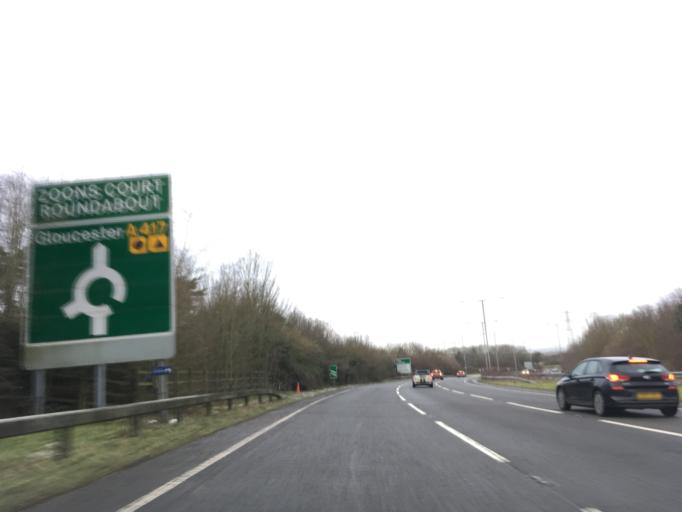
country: GB
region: England
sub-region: Gloucestershire
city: Barnwood
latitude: 51.8594
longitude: -2.1813
